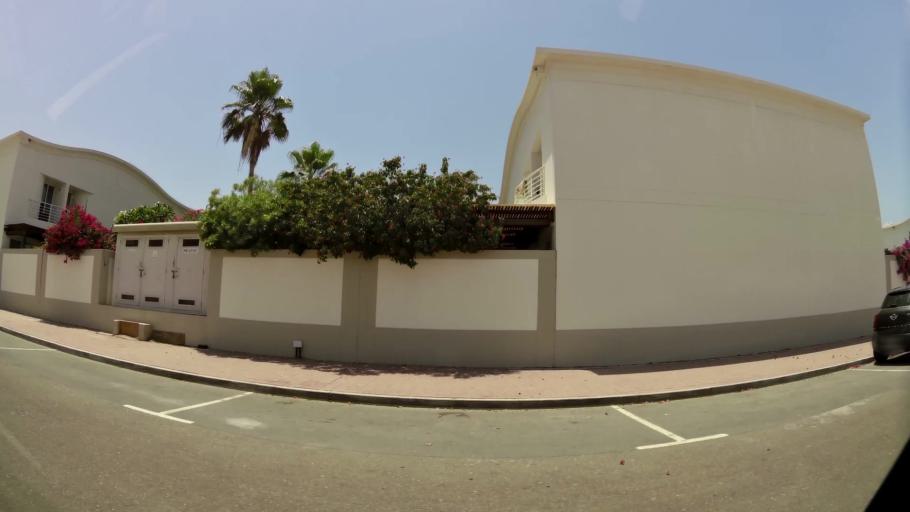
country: AE
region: Dubai
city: Dubai
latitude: 25.1992
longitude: 55.2461
